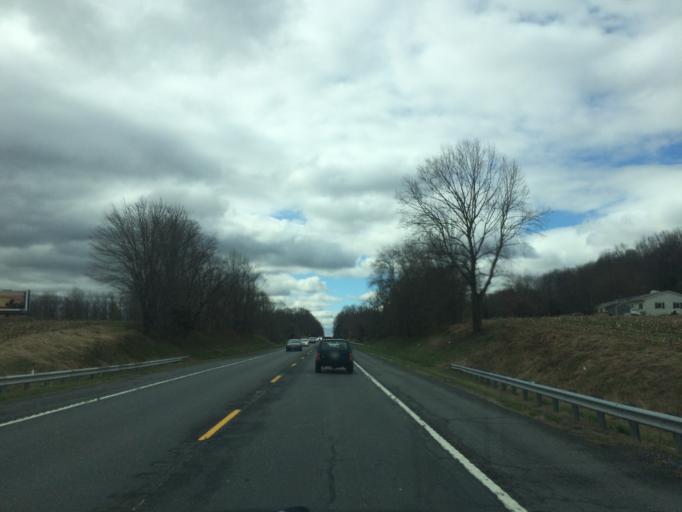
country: US
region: Maryland
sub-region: Frederick County
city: Jefferson
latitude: 39.3513
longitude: -77.5054
